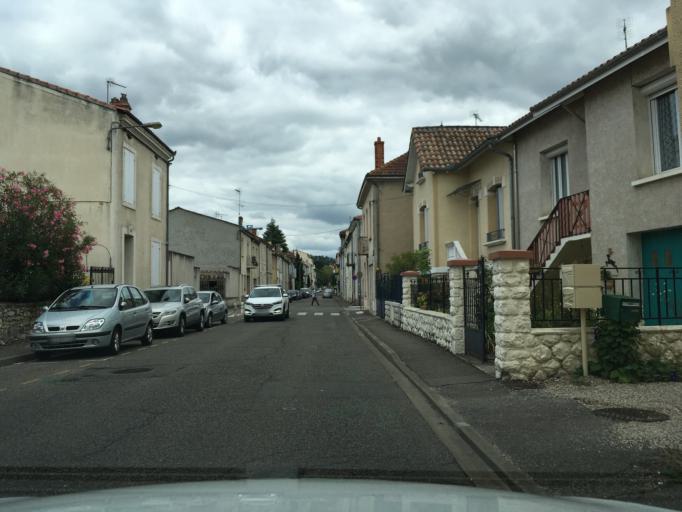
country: FR
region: Aquitaine
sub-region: Departement du Lot-et-Garonne
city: Le Passage
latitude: 44.1939
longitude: 0.6169
